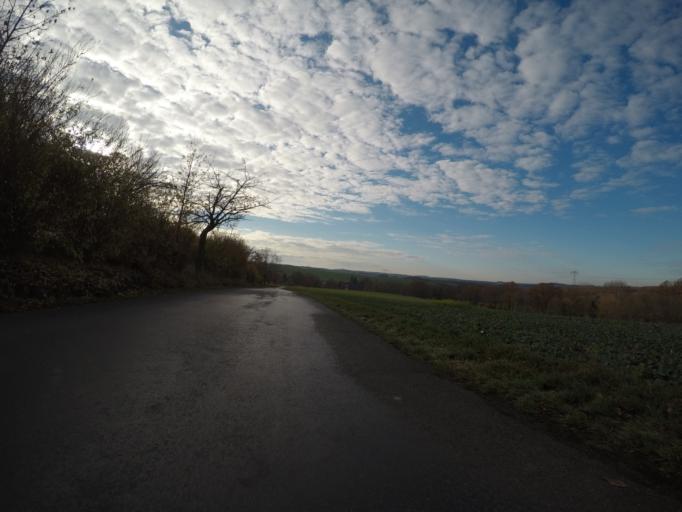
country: DE
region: Thuringia
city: Vollmershain
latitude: 50.8558
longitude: 12.2924
